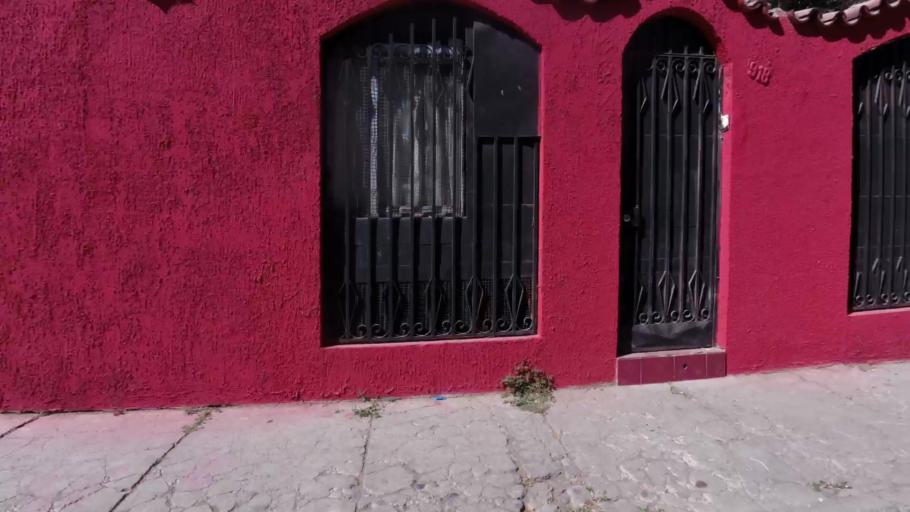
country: CL
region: O'Higgins
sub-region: Provincia de Cachapoal
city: Rancagua
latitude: -34.1755
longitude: -70.7468
